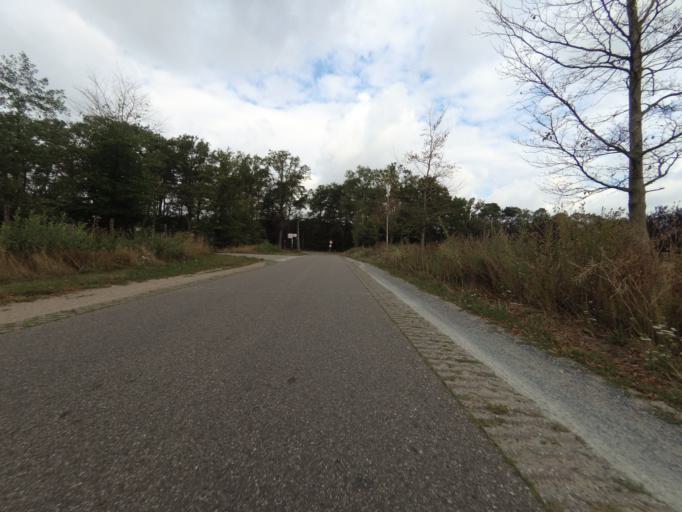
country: NL
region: Overijssel
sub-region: Gemeente Borne
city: Borne
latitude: 52.3169
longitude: 6.7712
